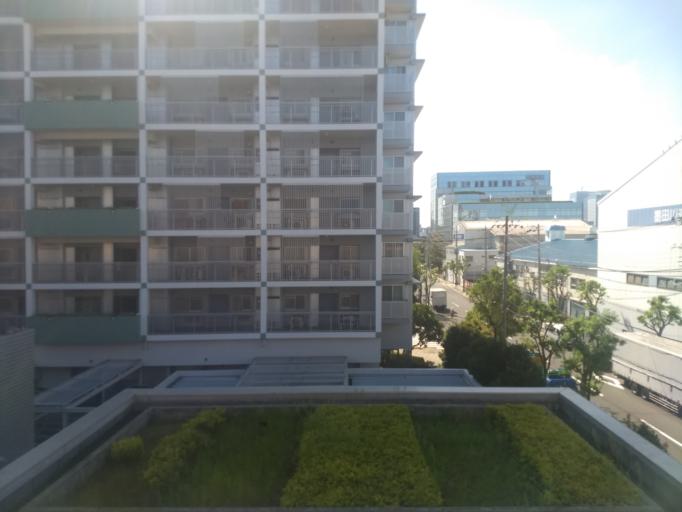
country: JP
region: Tokyo
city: Urayasu
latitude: 35.6595
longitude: 139.8164
